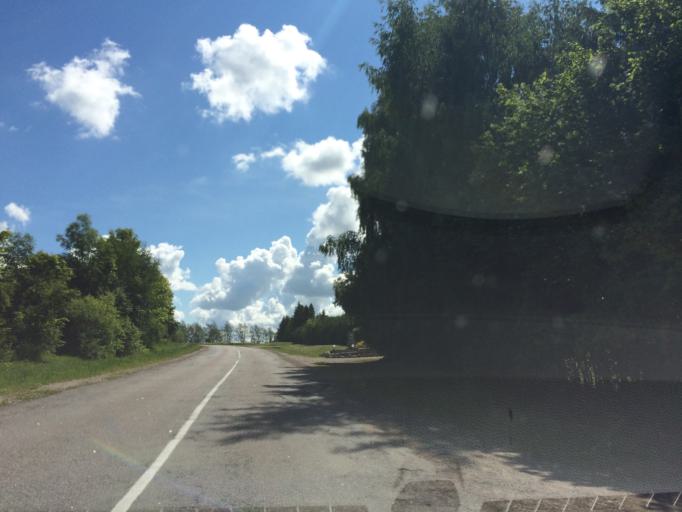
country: LV
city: Tervete
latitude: 56.4778
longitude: 23.3867
